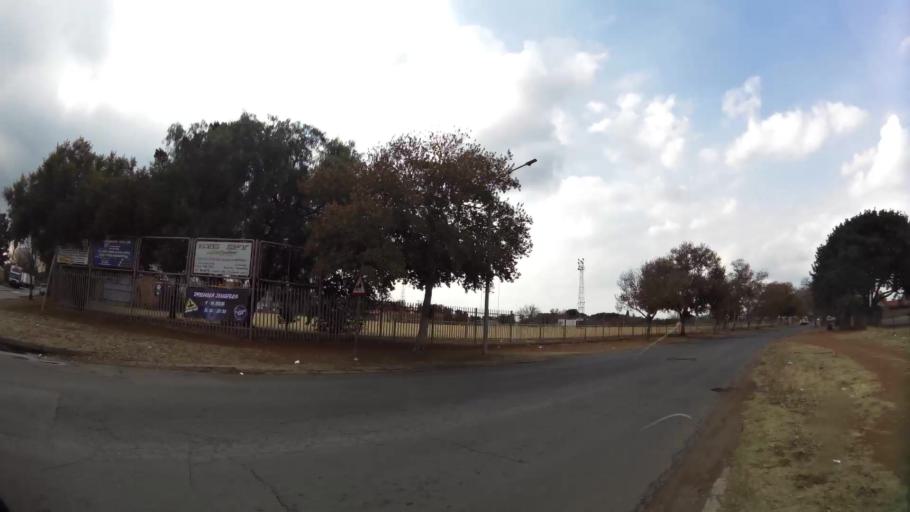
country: ZA
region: Gauteng
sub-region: Sedibeng District Municipality
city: Vanderbijlpark
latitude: -26.7252
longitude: 27.8461
